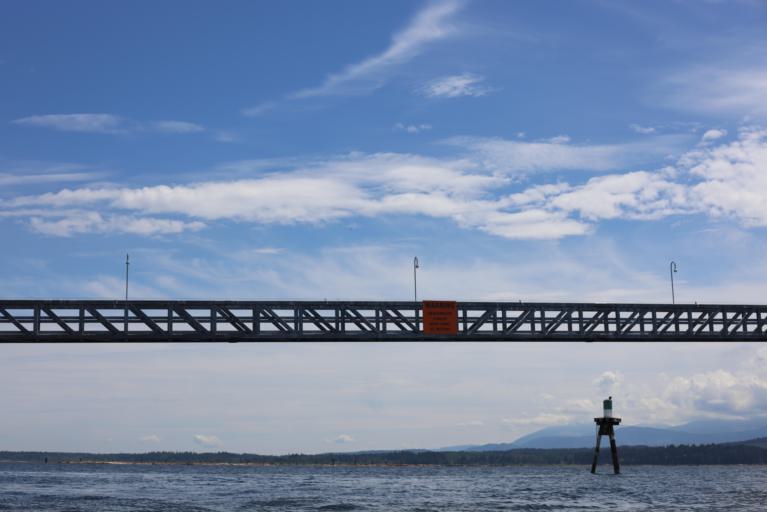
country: CA
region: British Columbia
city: Nanaimo
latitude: 49.1654
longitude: -123.9255
